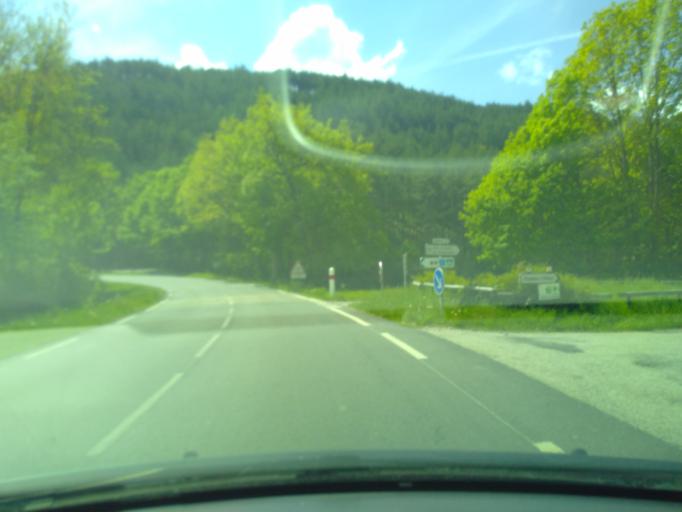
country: FR
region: Rhone-Alpes
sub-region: Departement de la Drome
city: Die
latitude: 44.5990
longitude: 5.4589
